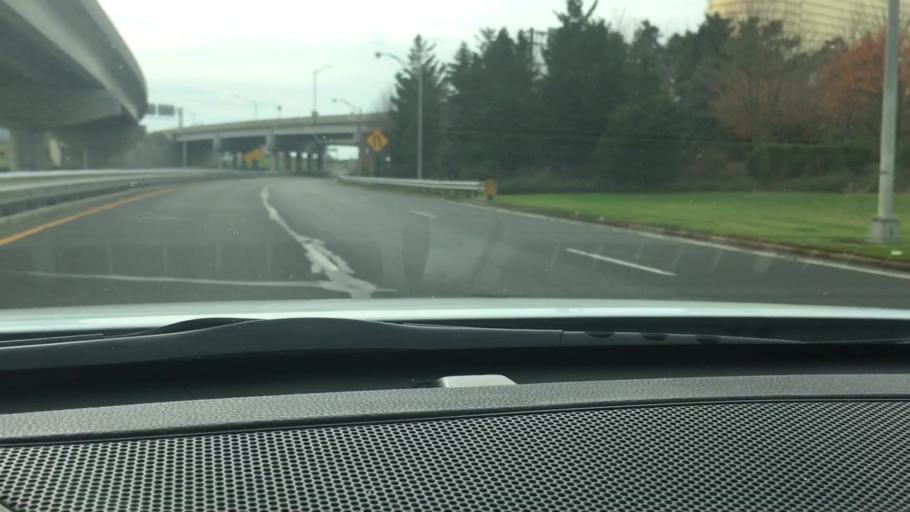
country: US
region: New Jersey
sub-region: Atlantic County
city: Atlantic City
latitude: 39.3782
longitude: -74.4311
